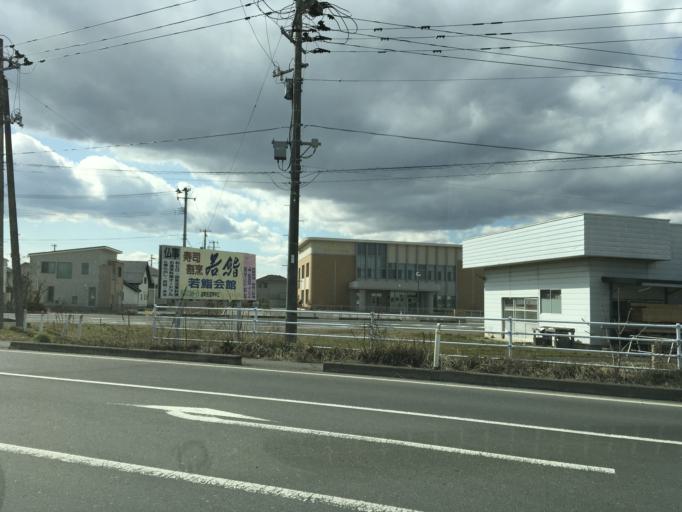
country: JP
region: Miyagi
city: Wakuya
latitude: 38.7075
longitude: 141.2163
